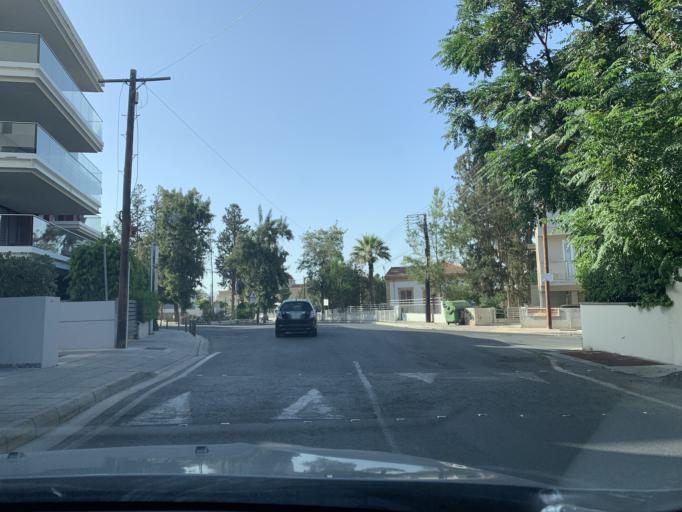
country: CY
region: Lefkosia
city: Nicosia
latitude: 35.1542
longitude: 33.3935
